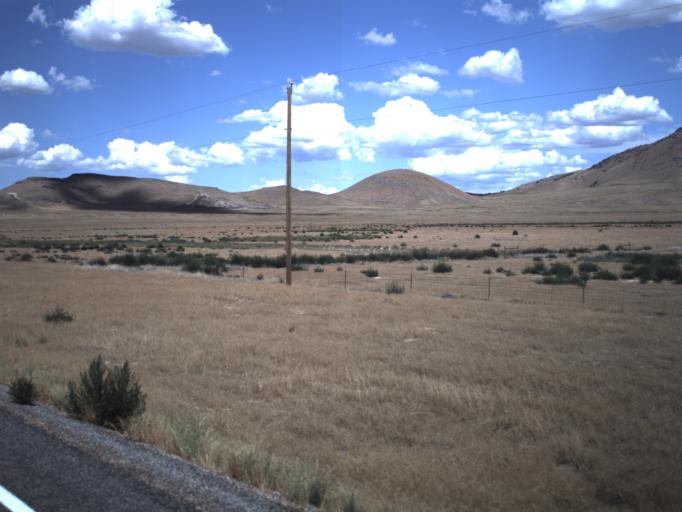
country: US
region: Utah
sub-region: Millard County
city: Delta
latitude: 39.6352
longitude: -112.3072
